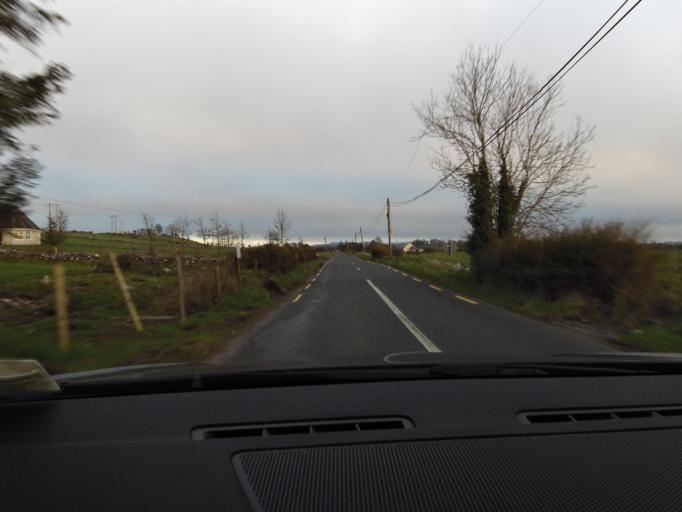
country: IE
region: Connaught
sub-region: Sligo
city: Ballymote
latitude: 54.0193
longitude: -8.5619
